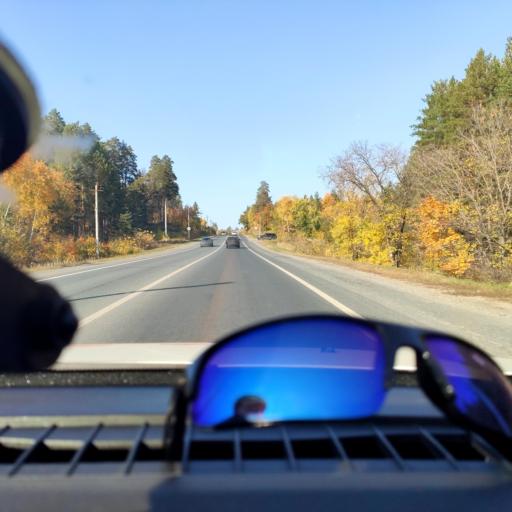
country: RU
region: Samara
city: Volzhskiy
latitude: 53.4425
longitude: 50.1235
